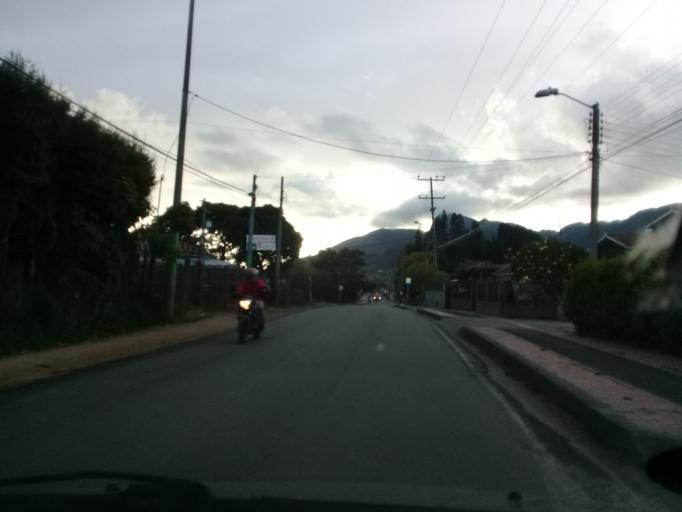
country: CO
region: Cundinamarca
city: Tabio
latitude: 4.9219
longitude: -74.0866
